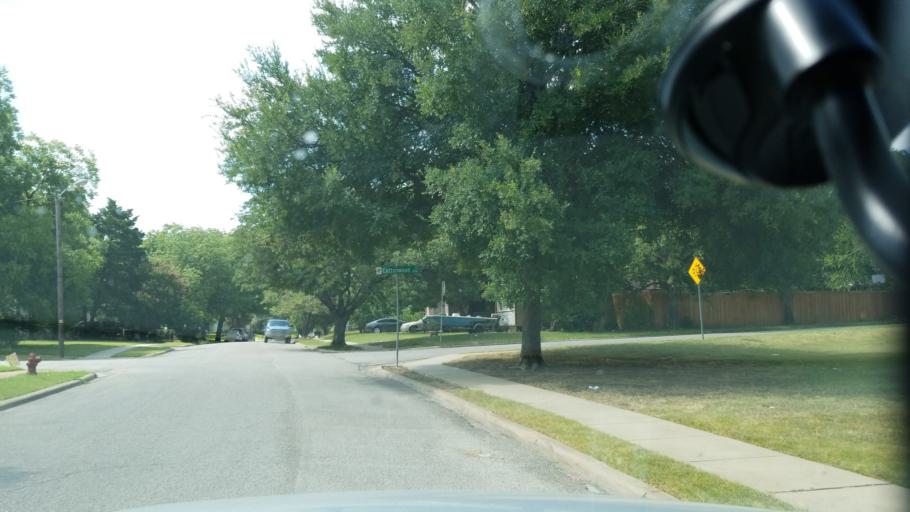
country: US
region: Texas
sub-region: Dallas County
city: Grand Prairie
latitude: 32.7563
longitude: -96.9771
